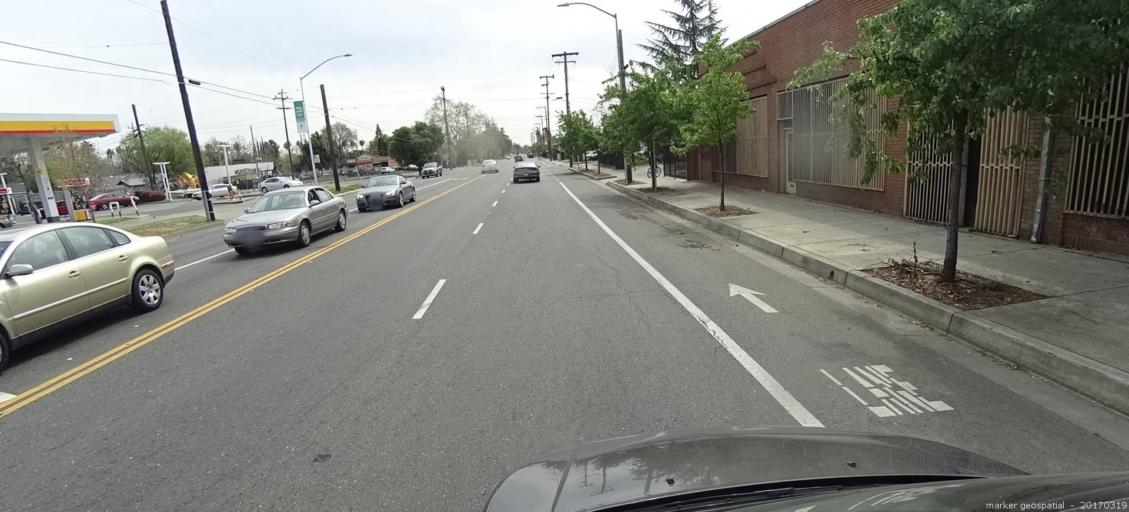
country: US
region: California
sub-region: Sacramento County
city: Parkway
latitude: 38.5394
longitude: -121.4498
